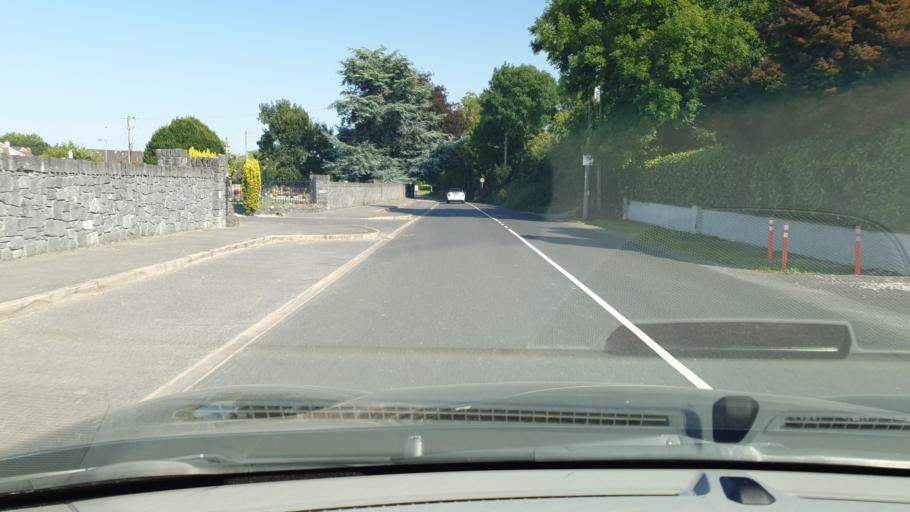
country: IE
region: Leinster
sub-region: An Mhi
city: Athboy
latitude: 53.6221
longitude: -6.9300
